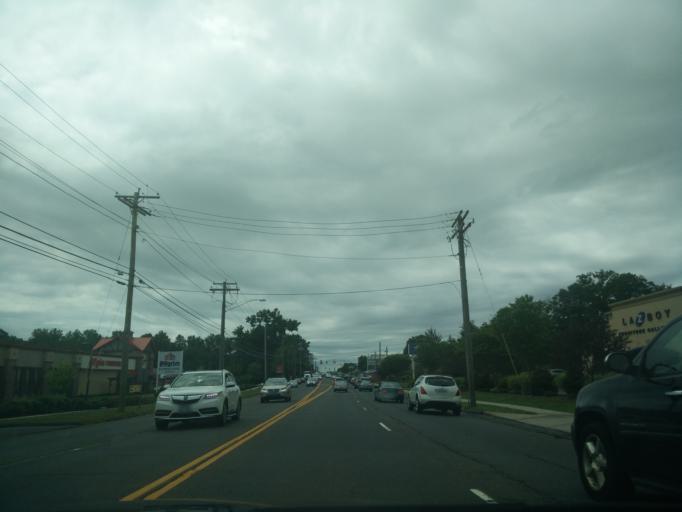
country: US
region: Connecticut
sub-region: New Haven County
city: Orange
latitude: 41.2502
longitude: -73.0220
